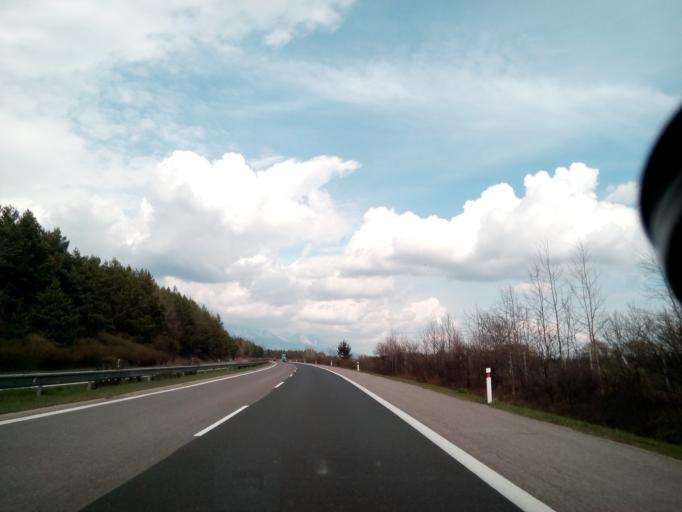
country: SK
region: Zilinsky
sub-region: Okres Liptovsky Mikulas
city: Hybe
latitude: 49.0518
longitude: 19.7929
